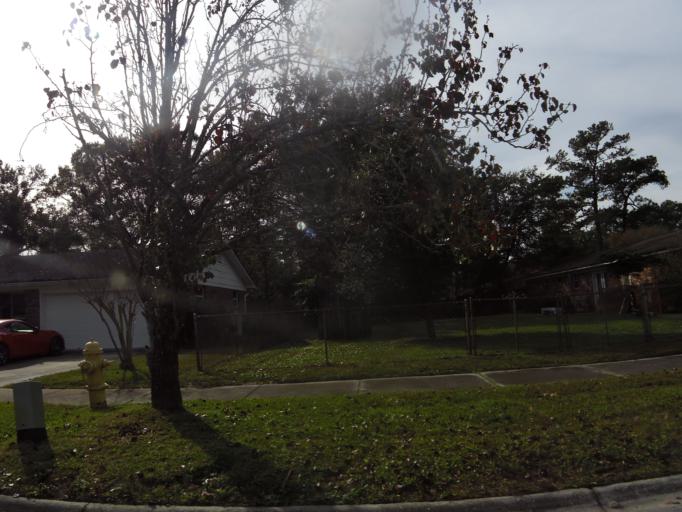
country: US
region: Florida
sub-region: Duval County
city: Jacksonville
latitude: 30.2274
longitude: -81.5946
